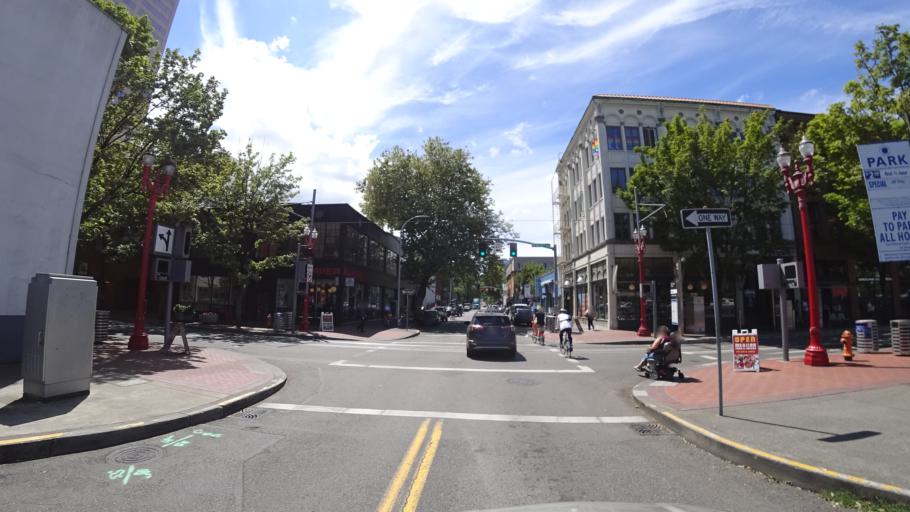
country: US
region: Oregon
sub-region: Multnomah County
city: Portland
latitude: 45.5238
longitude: -122.6752
